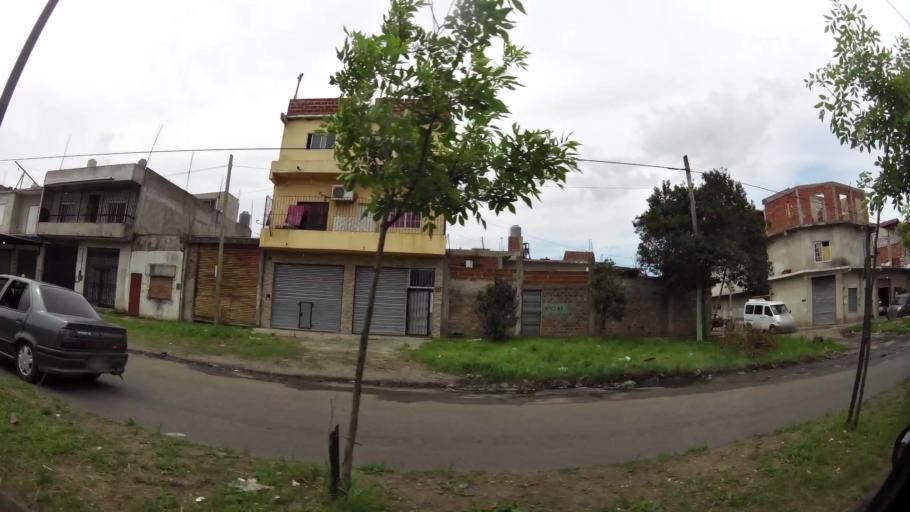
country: AR
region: Buenos Aires
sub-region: Partido de Quilmes
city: Quilmes
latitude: -34.7570
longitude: -58.2573
